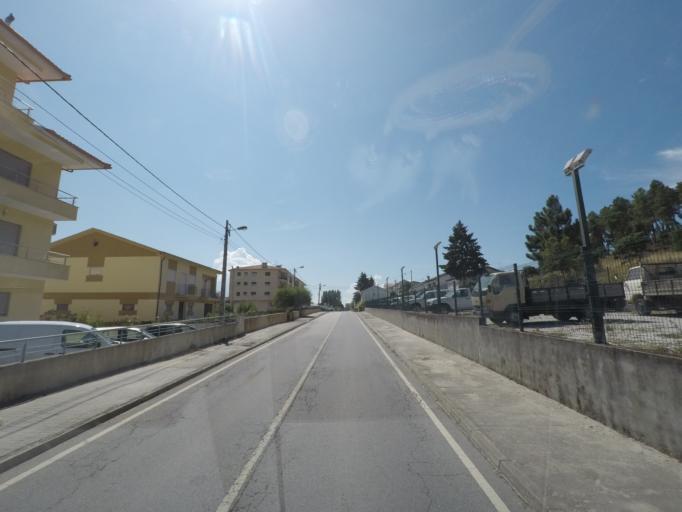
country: PT
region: Vila Real
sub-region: Sabrosa
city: Sabrosa
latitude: 41.2680
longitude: -7.4793
